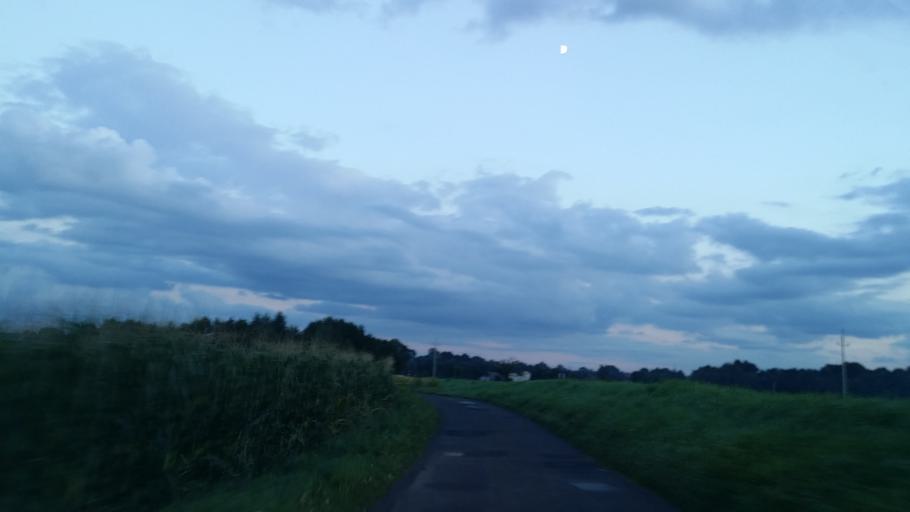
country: PL
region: Lesser Poland Voivodeship
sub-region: Powiat oswiecimski
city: Przeciszow
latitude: 50.0141
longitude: 19.3794
